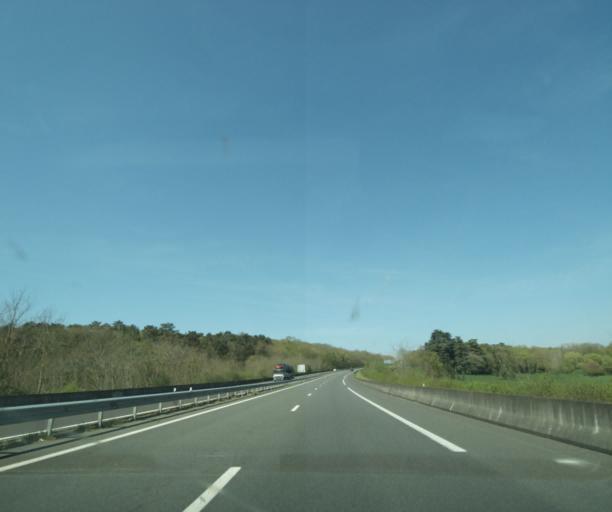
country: FR
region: Bourgogne
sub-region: Departement de la Nievre
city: Pouilly-sur-Loire
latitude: 47.2904
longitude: 2.9581
